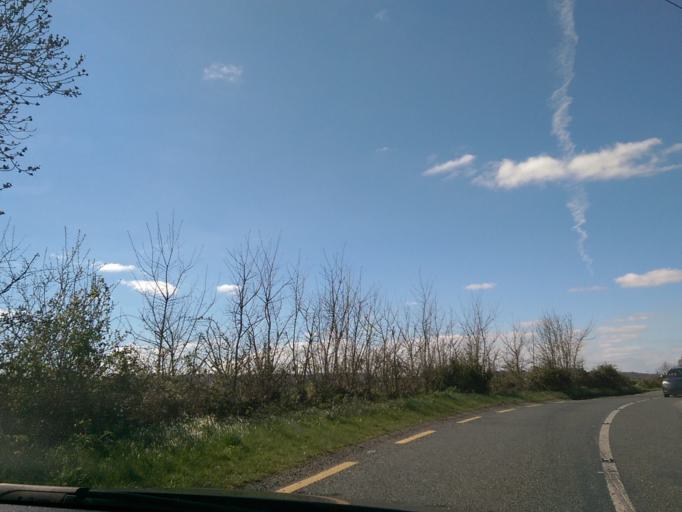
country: IE
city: Ballylinan
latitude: 53.0015
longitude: -7.0543
